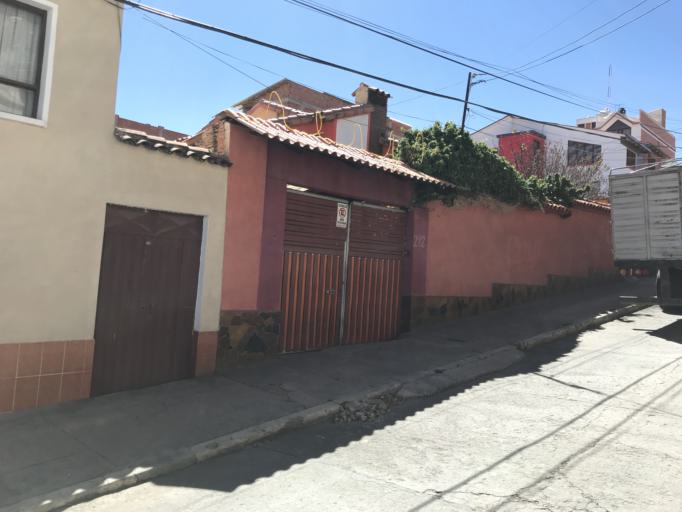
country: BO
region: Chuquisaca
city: Sucre
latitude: -19.0391
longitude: -65.2506
